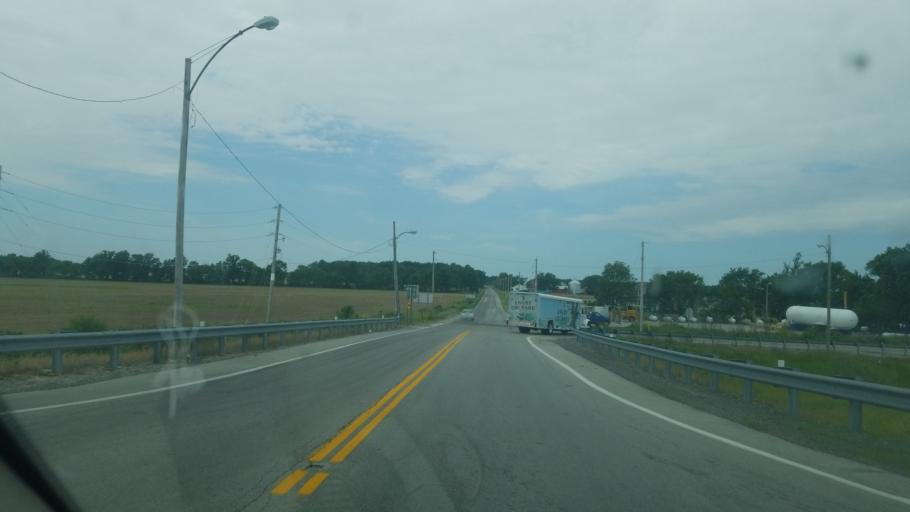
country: US
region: Ohio
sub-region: Wood County
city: North Baltimore
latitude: 41.2405
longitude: -83.6549
